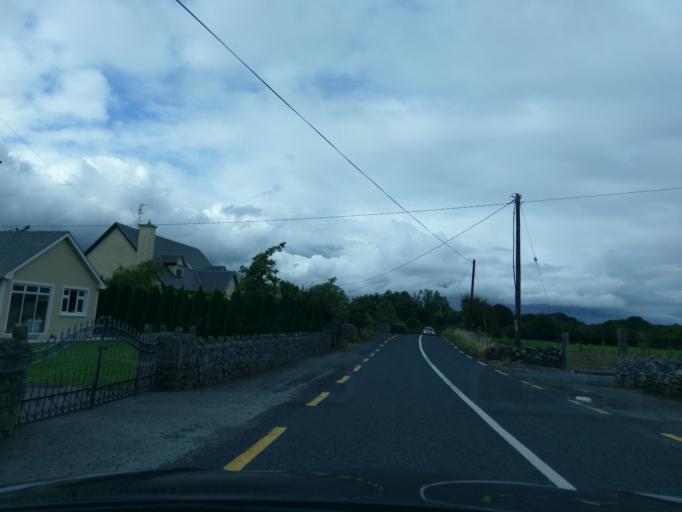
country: IE
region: Connaught
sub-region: County Galway
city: Athenry
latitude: 53.2530
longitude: -8.7453
